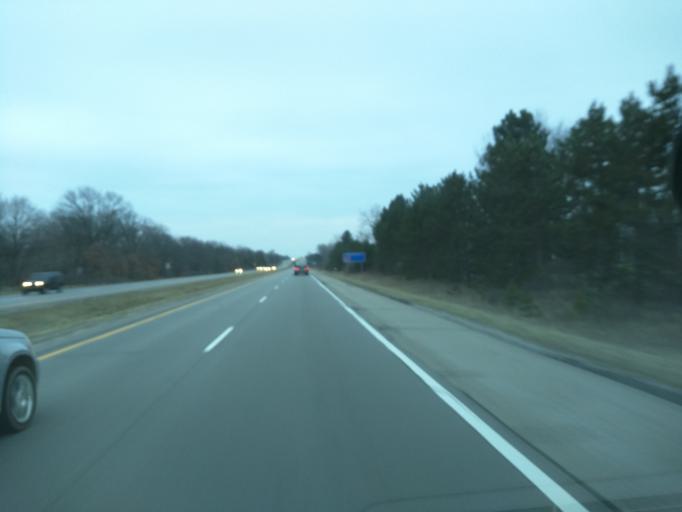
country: US
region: Michigan
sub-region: Ingham County
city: Leslie
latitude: 42.3929
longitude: -84.4293
